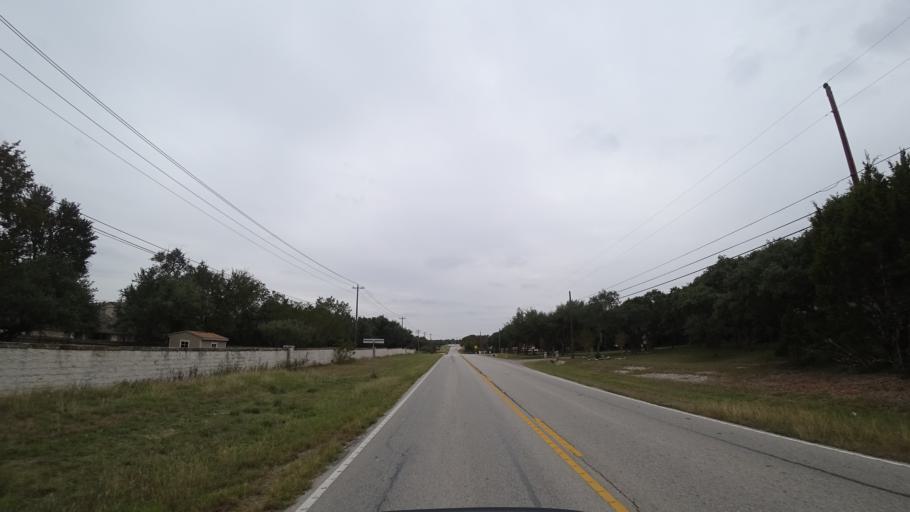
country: US
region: Texas
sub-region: Travis County
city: Shady Hollow
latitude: 30.1974
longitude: -97.9216
